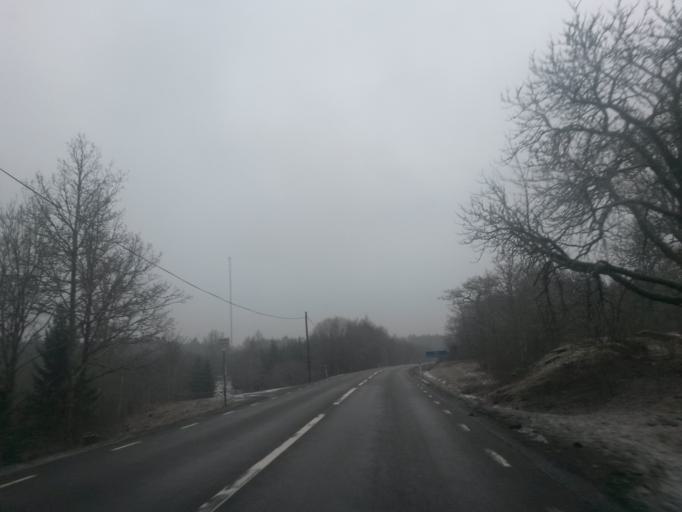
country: SE
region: Vaestra Goetaland
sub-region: Alingsas Kommun
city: Sollebrunn
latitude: 58.1753
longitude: 12.4167
